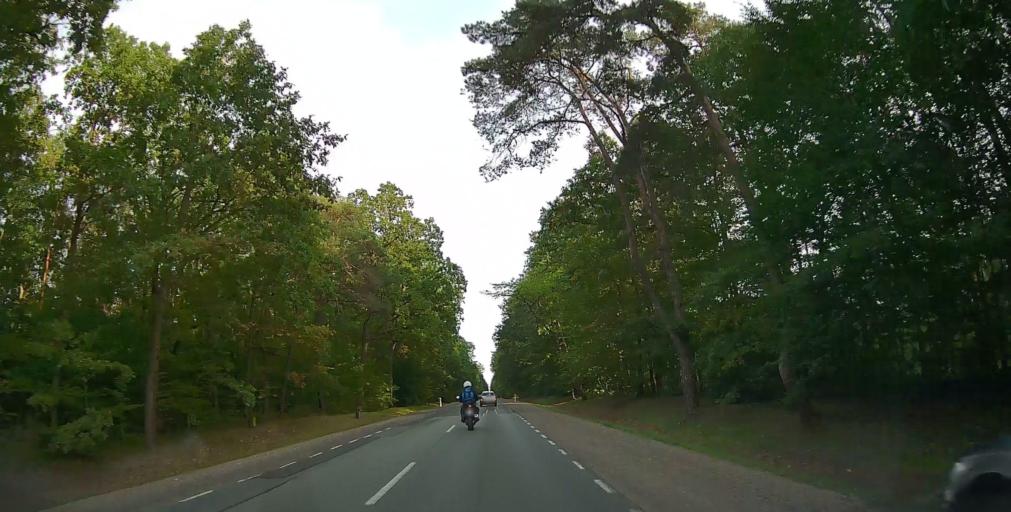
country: PL
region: Masovian Voivodeship
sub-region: Powiat piaseczynski
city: Zabieniec
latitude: 52.0487
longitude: 21.0693
